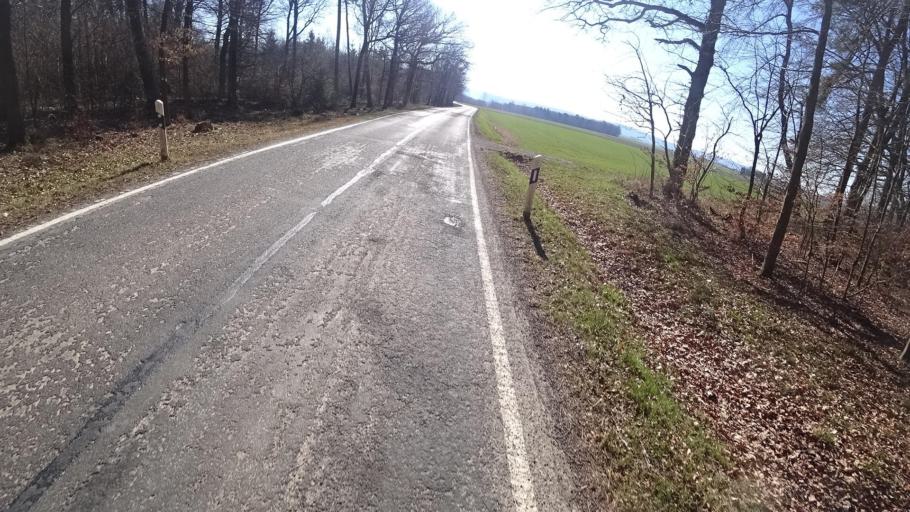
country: DE
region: Rheinland-Pfalz
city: Mutterschied
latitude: 49.9893
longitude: 7.5762
